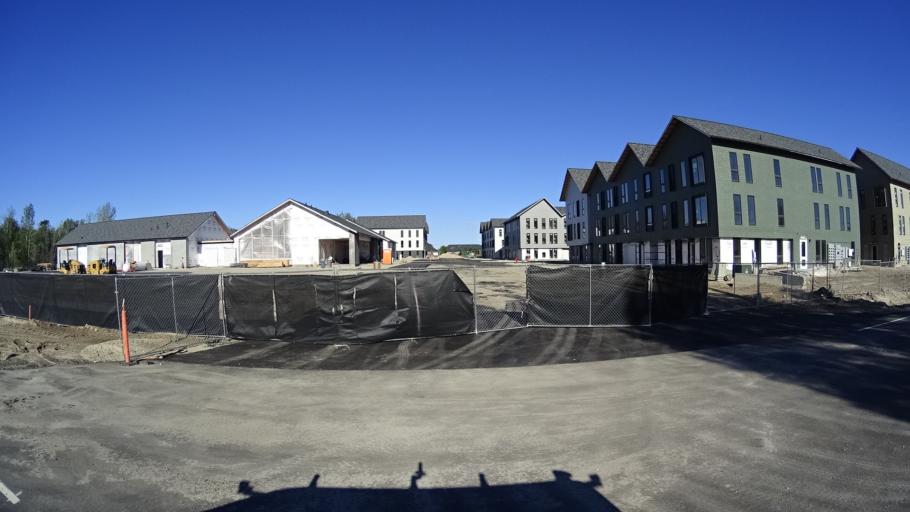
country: US
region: Idaho
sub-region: Ada County
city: Eagle
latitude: 43.6914
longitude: -116.4136
